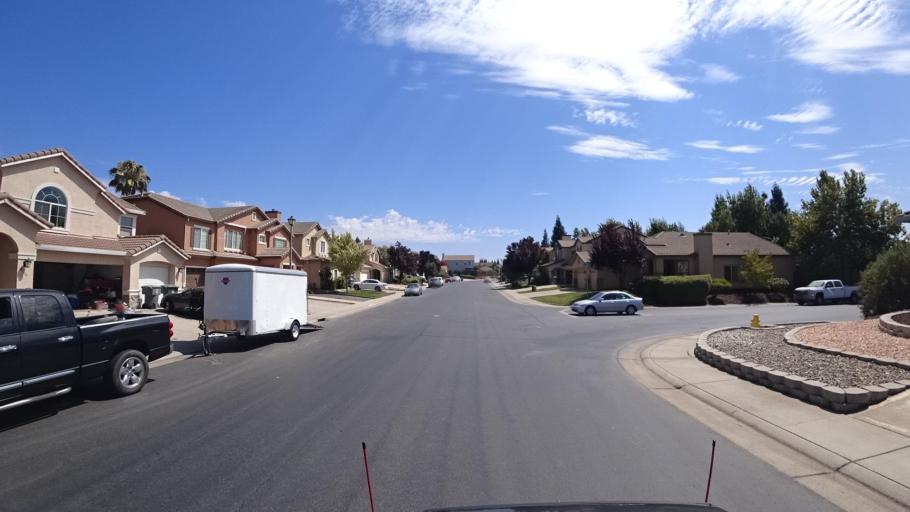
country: US
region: California
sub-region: Placer County
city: Roseville
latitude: 38.8031
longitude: -121.2906
